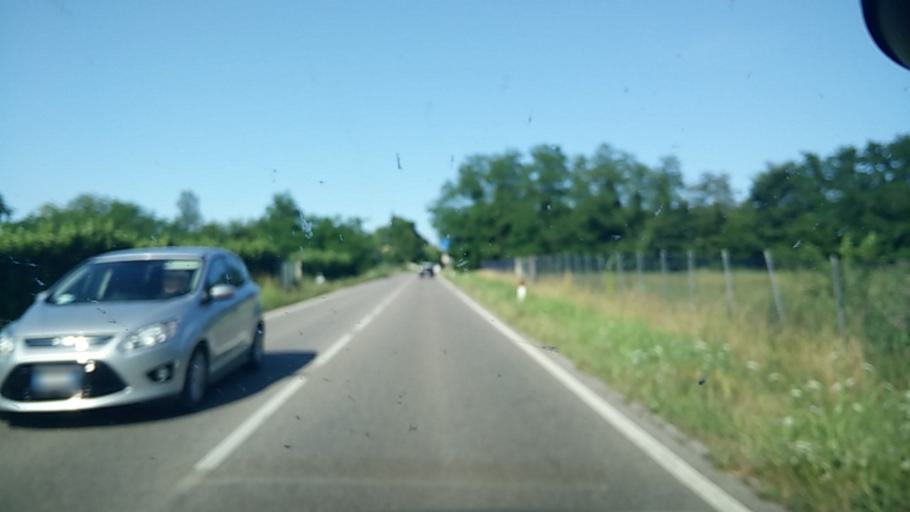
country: IT
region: Veneto
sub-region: Provincia di Treviso
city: Carbonera
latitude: 45.6799
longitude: 12.2955
